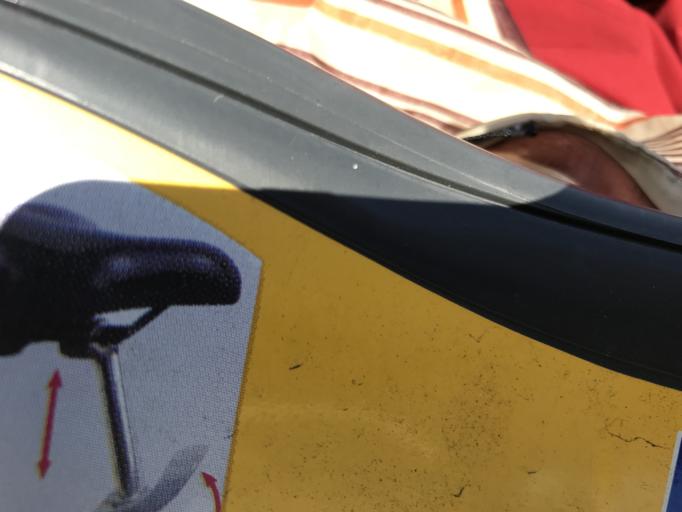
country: AU
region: Queensland
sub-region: Brisbane
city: Brisbane
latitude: -27.4742
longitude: 153.0345
